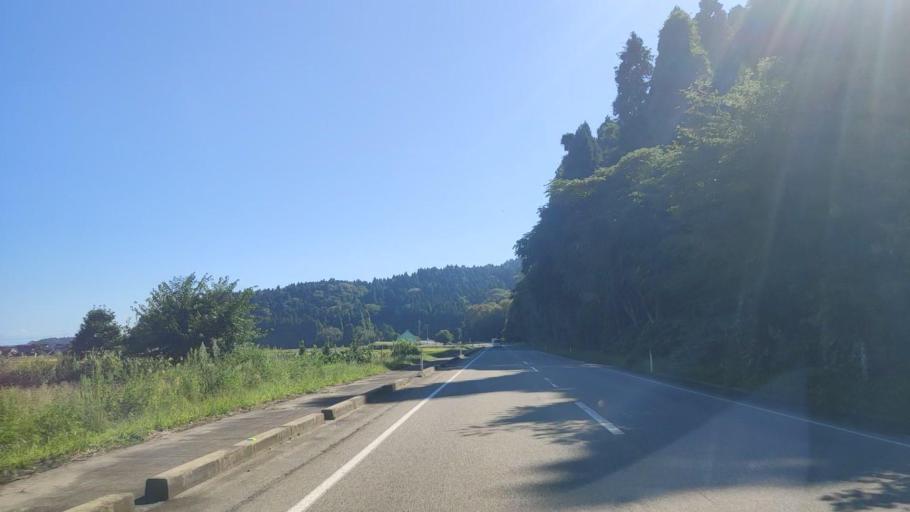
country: JP
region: Ishikawa
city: Nanao
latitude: 37.3897
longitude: 137.2336
